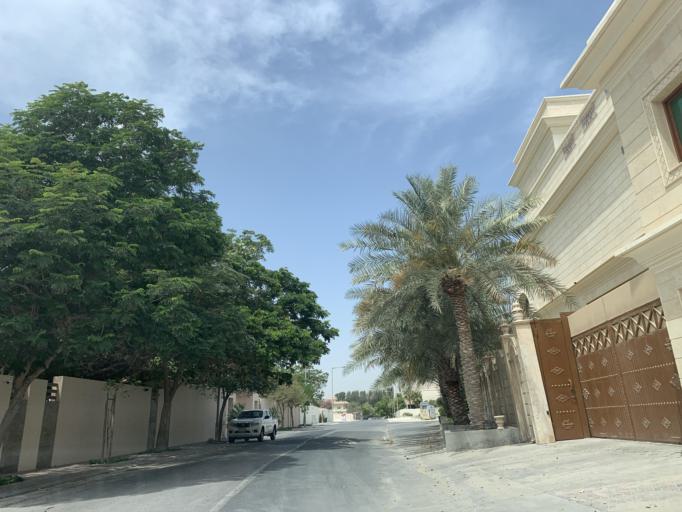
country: BH
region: Northern
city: Ar Rifa'
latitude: 26.1433
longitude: 50.5580
